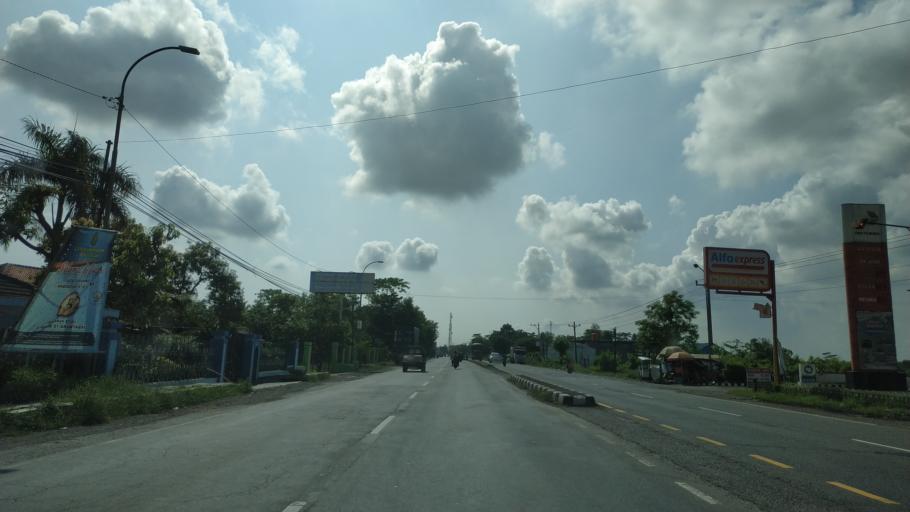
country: ID
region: Central Java
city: Comal
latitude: -6.8853
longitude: 109.5573
